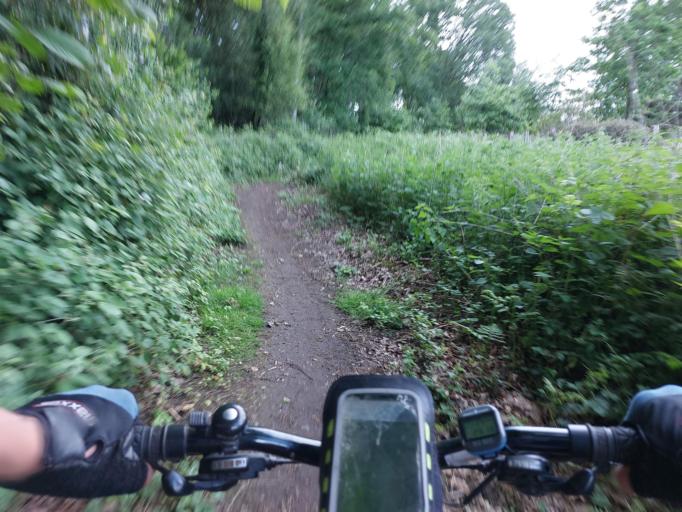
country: BE
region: Wallonia
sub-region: Province du Hainaut
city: Beloeil
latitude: 50.4919
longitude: 3.7604
